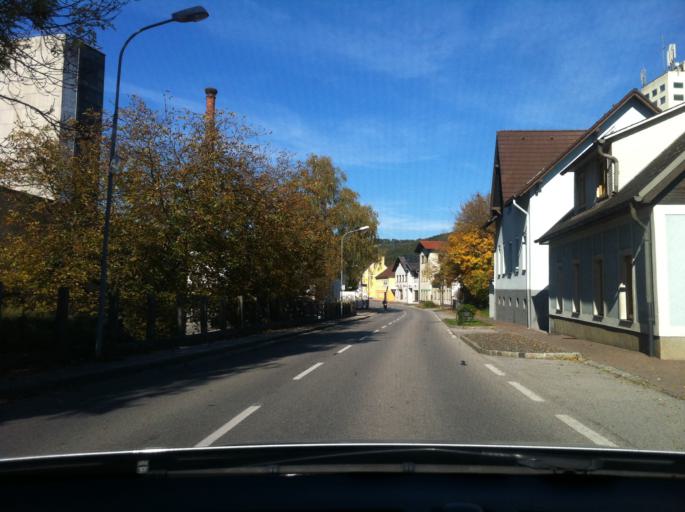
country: AT
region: Lower Austria
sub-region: Politischer Bezirk Neunkirchen
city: Grimmenstein
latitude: 47.6137
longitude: 16.1258
